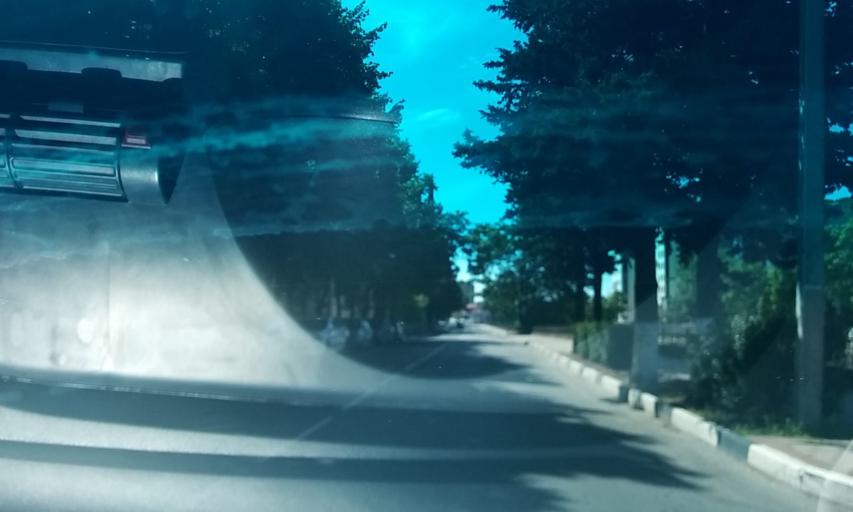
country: RU
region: Krasnodarskiy
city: Tuapse
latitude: 44.1049
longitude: 39.0587
